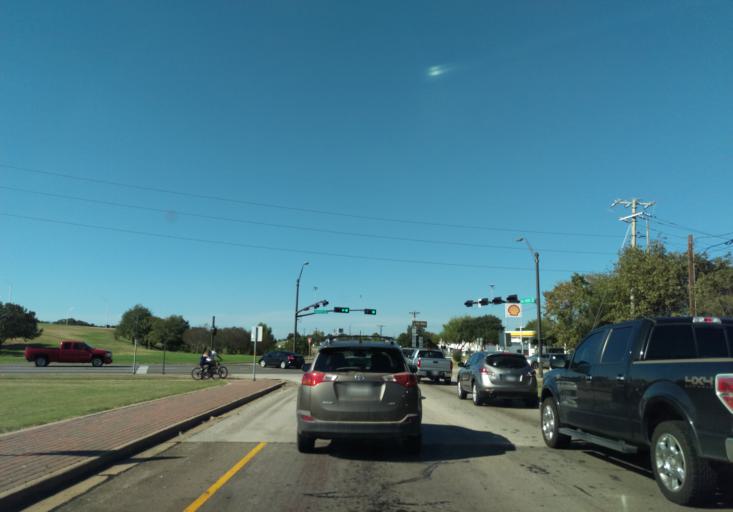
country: US
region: Texas
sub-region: Brazos County
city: College Station
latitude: 30.6301
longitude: -96.3012
